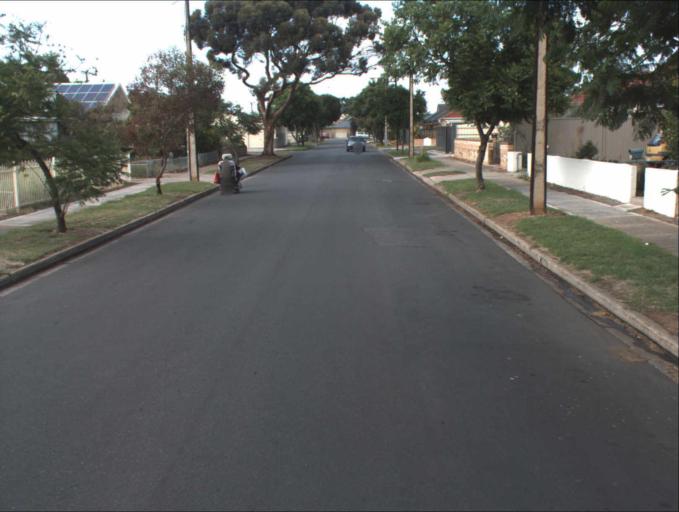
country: AU
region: South Australia
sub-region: Charles Sturt
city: Woodville North
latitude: -34.8689
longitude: 138.5492
